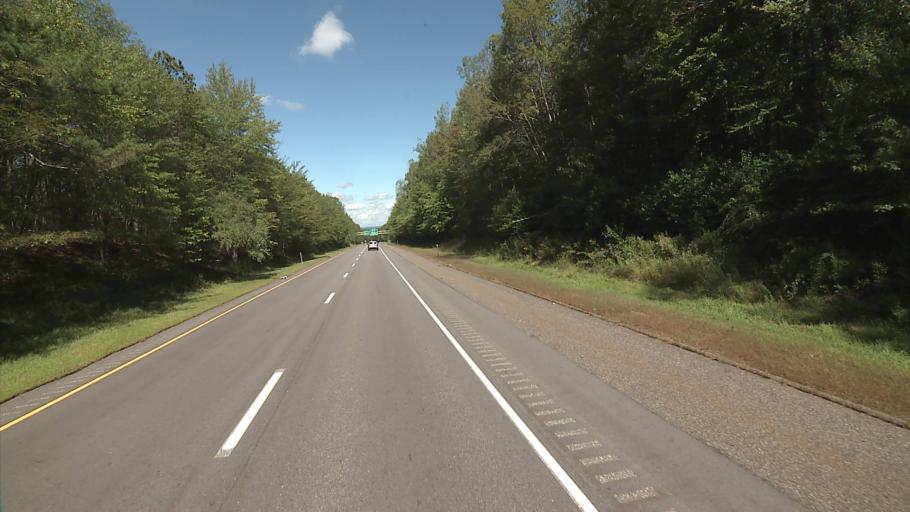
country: US
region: Connecticut
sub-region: New London County
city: Colchester
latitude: 41.5504
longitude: -72.3176
